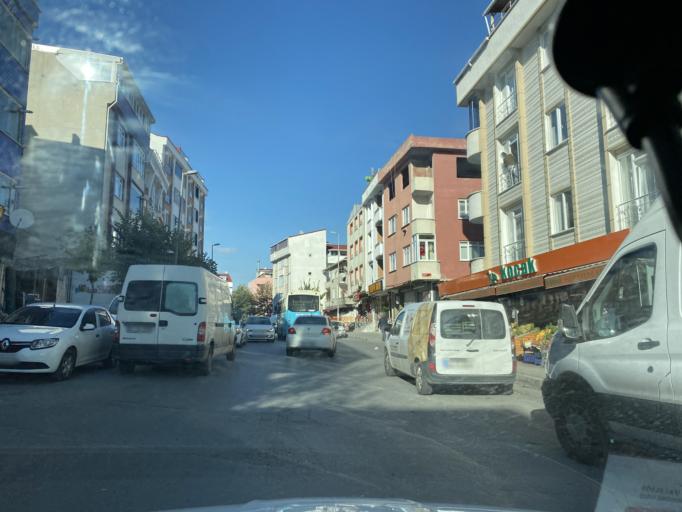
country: TR
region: Istanbul
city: Esenyurt
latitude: 41.0435
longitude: 28.6505
